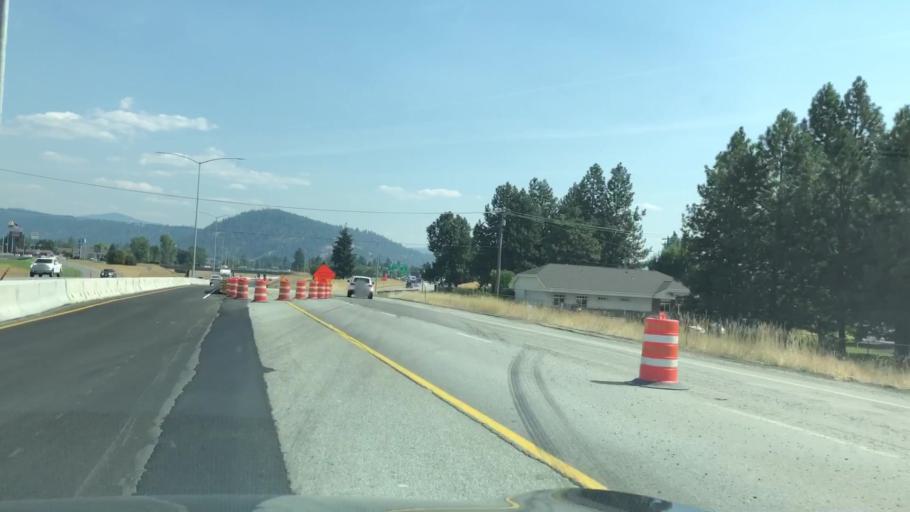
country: US
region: Idaho
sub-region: Kootenai County
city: Coeur d'Alene
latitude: 47.6989
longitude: -116.7972
